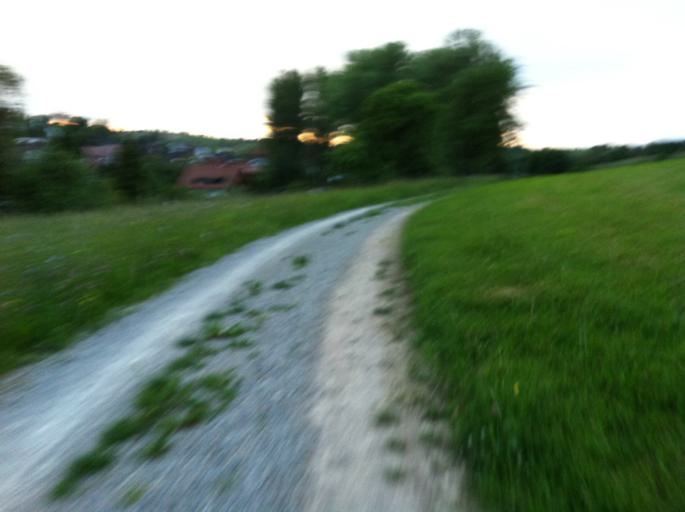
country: DE
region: Baden-Wuerttemberg
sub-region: Freiburg Region
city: Rheinfelden (Baden)
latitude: 47.5978
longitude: 7.7953
